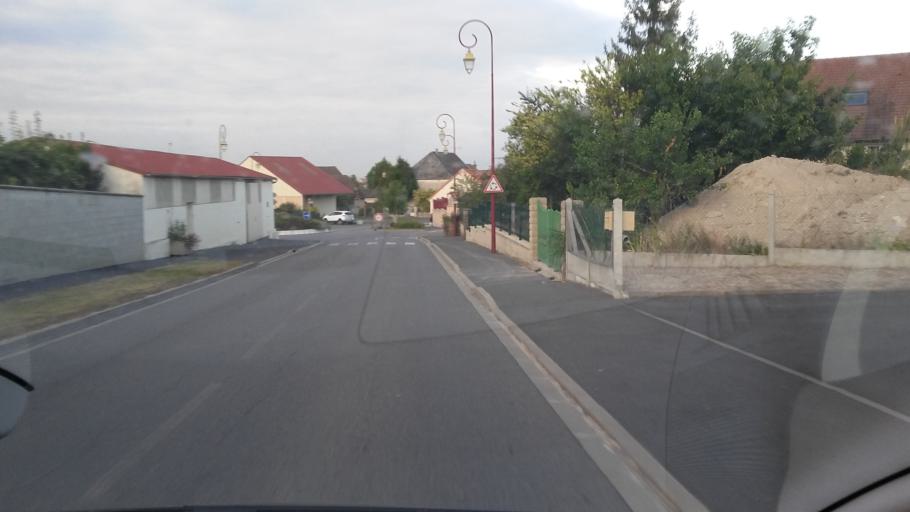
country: FR
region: Champagne-Ardenne
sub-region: Departement de la Marne
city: Vertus
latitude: 48.8766
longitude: 4.0001
